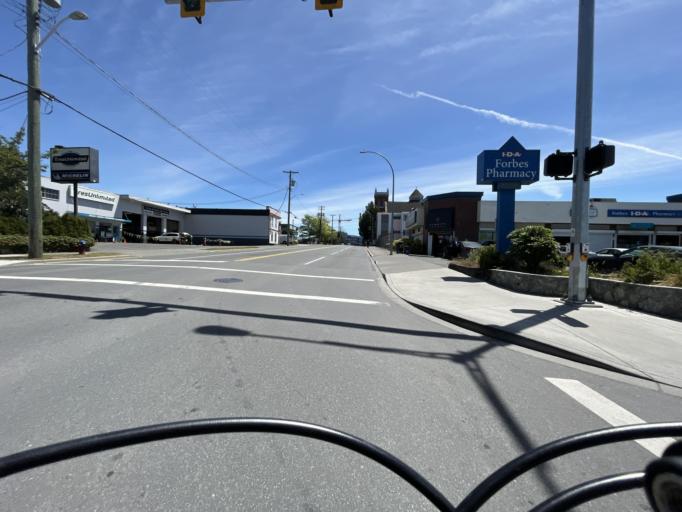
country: CA
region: British Columbia
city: Victoria
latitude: 48.4394
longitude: -123.3704
